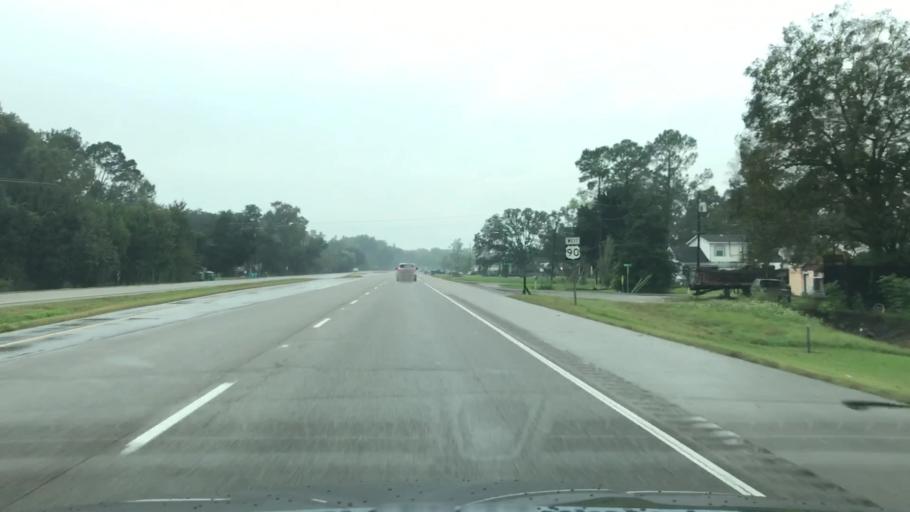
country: US
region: Louisiana
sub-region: Saint Charles Parish
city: Des Allemands
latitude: 29.8358
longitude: -90.4531
